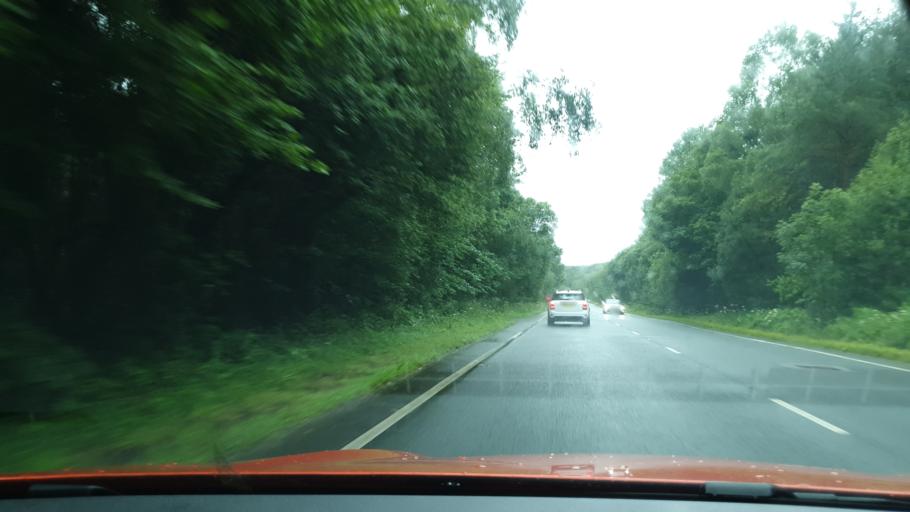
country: GB
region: England
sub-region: Cumbria
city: Ulverston
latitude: 54.2498
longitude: -3.0211
